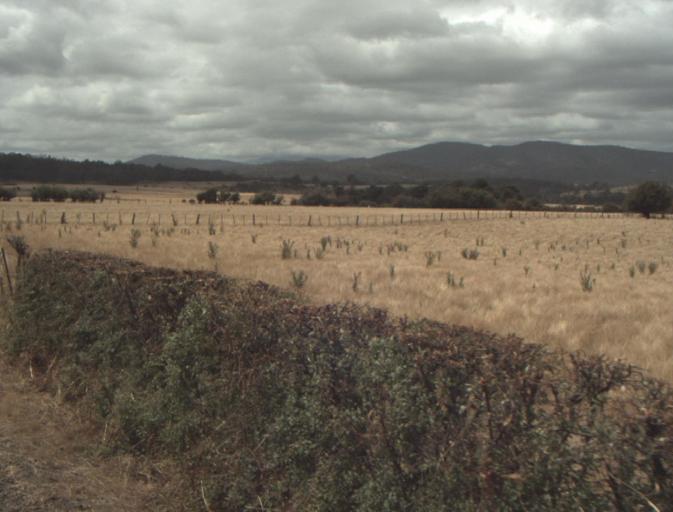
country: AU
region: Tasmania
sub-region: Northern Midlands
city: Evandale
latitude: -41.5207
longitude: 147.2840
